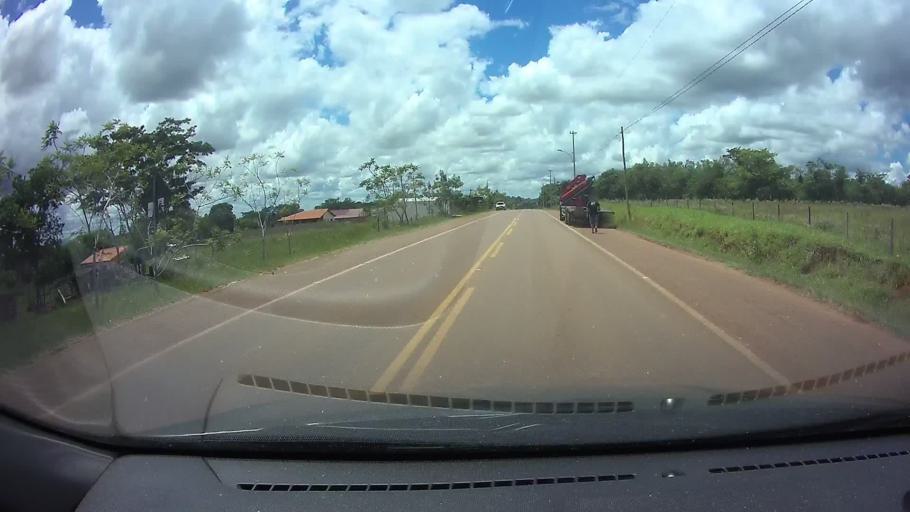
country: PY
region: Paraguari
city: La Colmena
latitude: -25.8930
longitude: -56.8411
